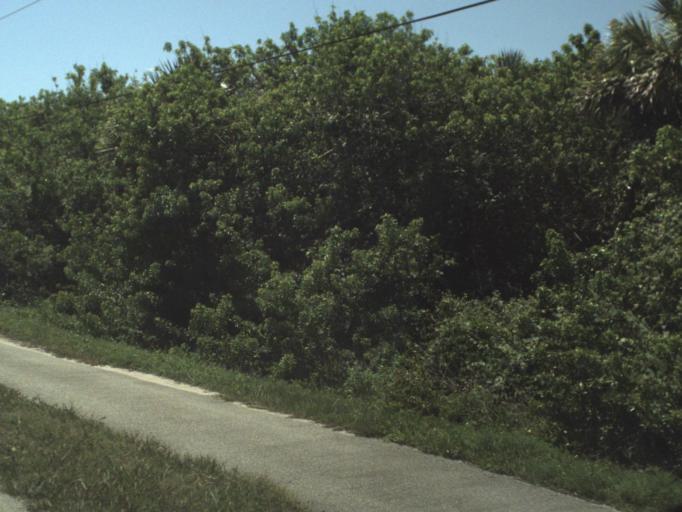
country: US
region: Florida
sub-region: Brevard County
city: Micco
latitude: 27.8847
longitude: -80.4613
